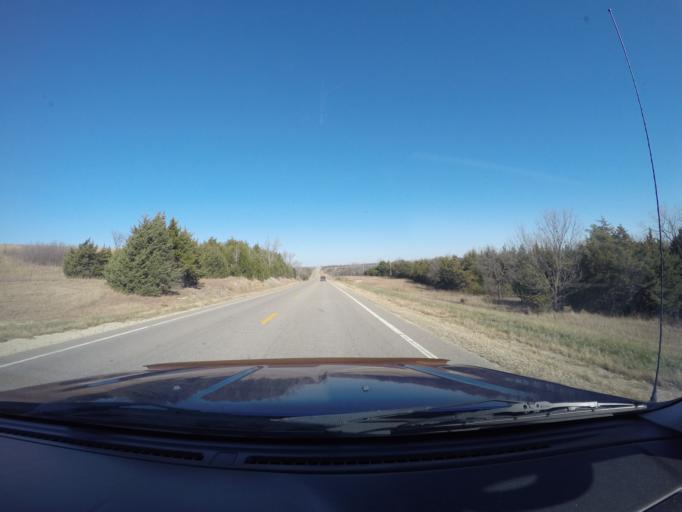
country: US
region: Kansas
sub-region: Riley County
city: Ogden
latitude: 39.3174
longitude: -96.7557
